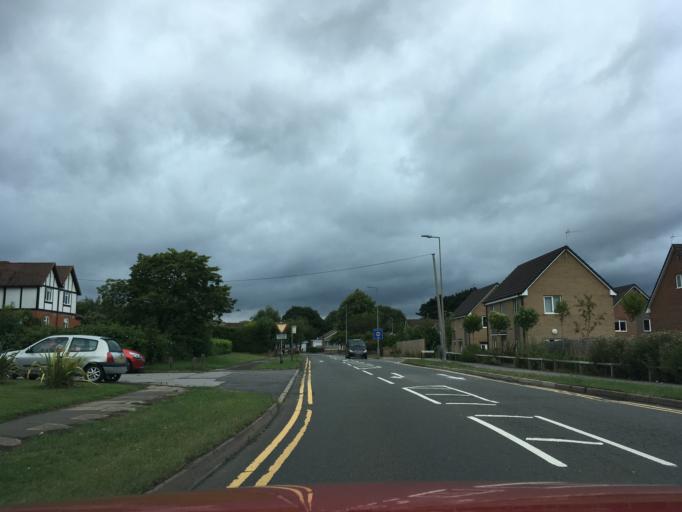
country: GB
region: England
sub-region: Buckinghamshire
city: Bletchley
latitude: 52.0024
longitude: -0.7401
